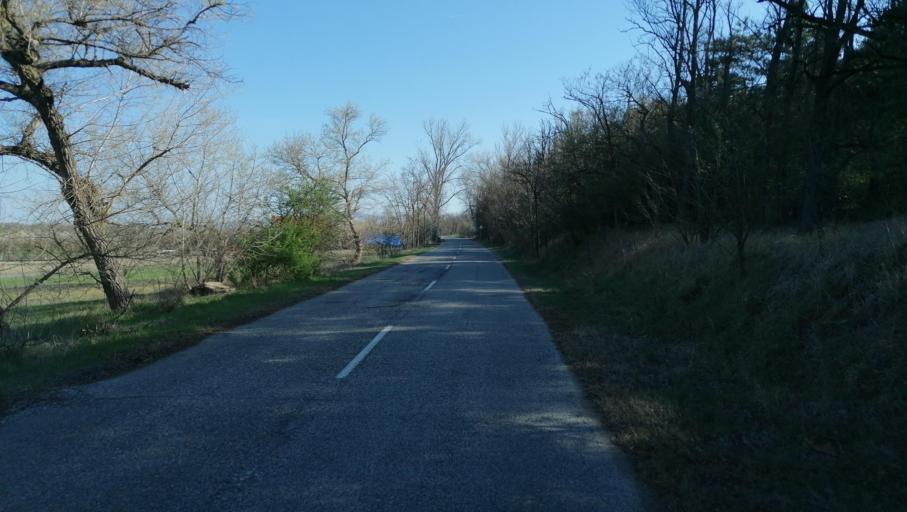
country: HU
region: Pest
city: Szentendre
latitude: 47.6816
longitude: 19.0963
